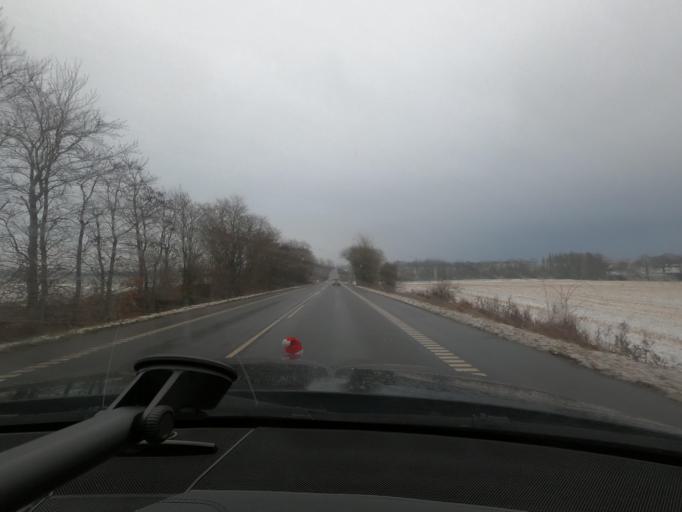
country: DK
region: South Denmark
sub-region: Sonderborg Kommune
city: Horuphav
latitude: 54.9094
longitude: 9.9208
